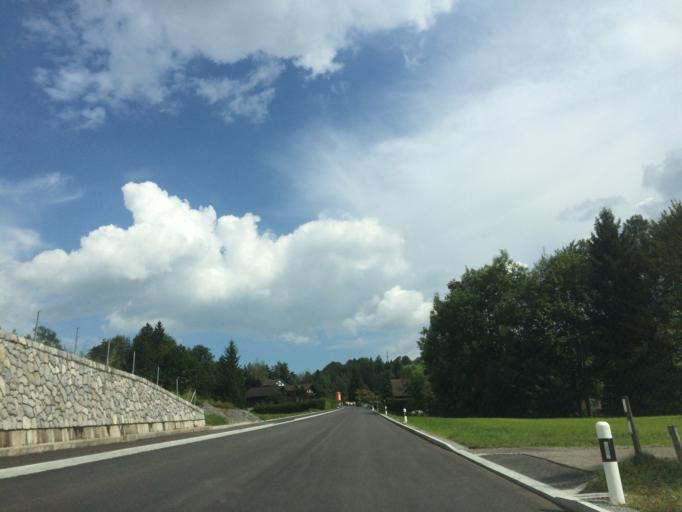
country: CH
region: Saint Gallen
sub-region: Wahlkreis Toggenburg
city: Wildhaus
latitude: 47.1985
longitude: 9.3143
